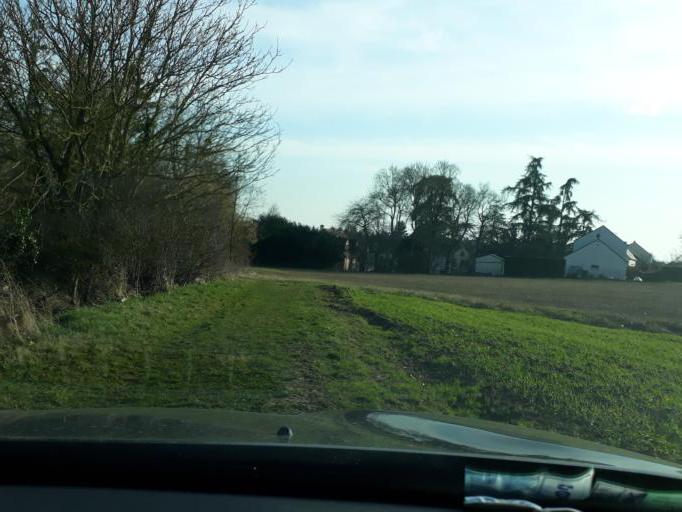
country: FR
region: Centre
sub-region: Departement du Loiret
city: Beaugency
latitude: 47.7905
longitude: 1.6249
